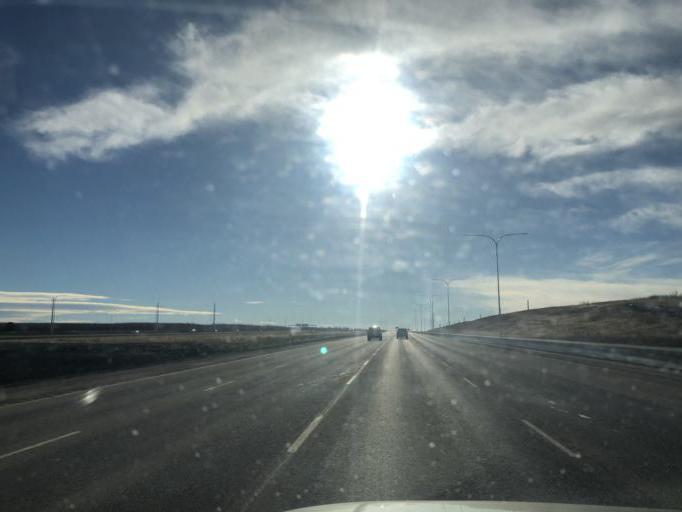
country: CA
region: Alberta
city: Calgary
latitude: 50.9756
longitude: -114.1575
